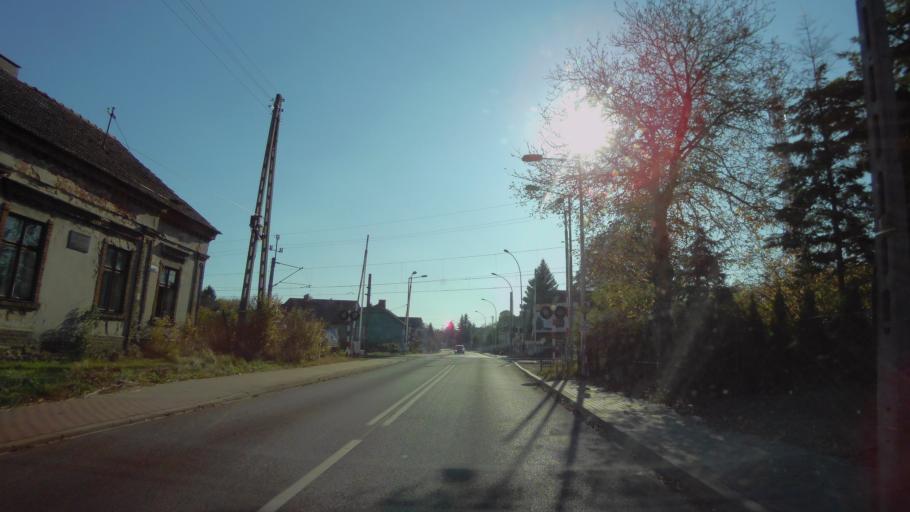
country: PL
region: Subcarpathian Voivodeship
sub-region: Powiat lezajski
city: Lezajsk
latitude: 50.2600
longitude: 22.4227
